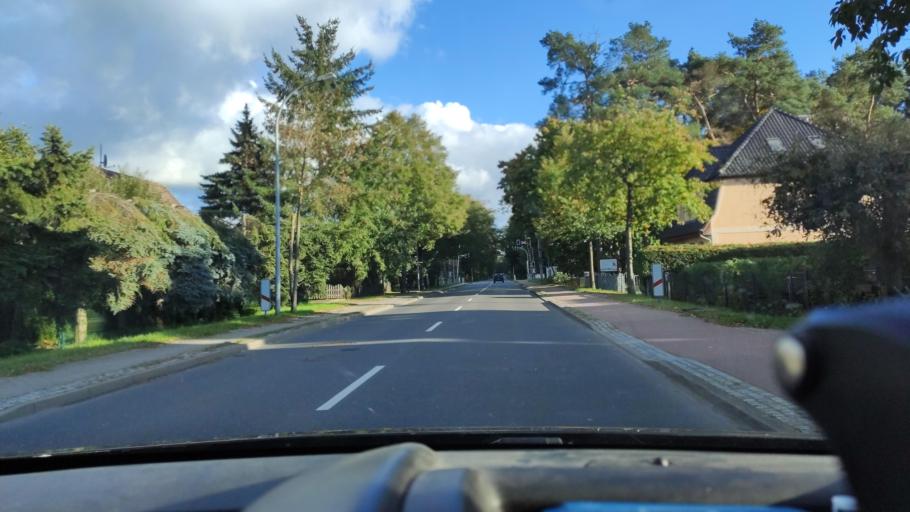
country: DE
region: Mecklenburg-Vorpommern
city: Muhl Rosin
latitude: 53.7753
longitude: 12.2486
